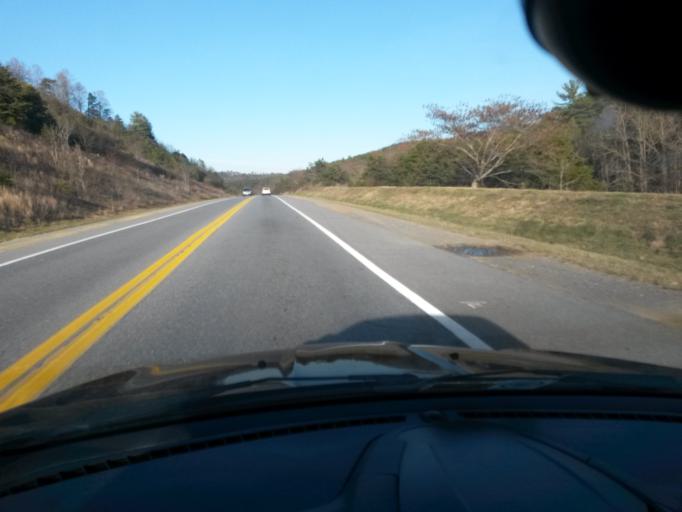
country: US
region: Virginia
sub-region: Alleghany County
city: Clifton Forge
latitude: 37.7623
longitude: -79.7866
